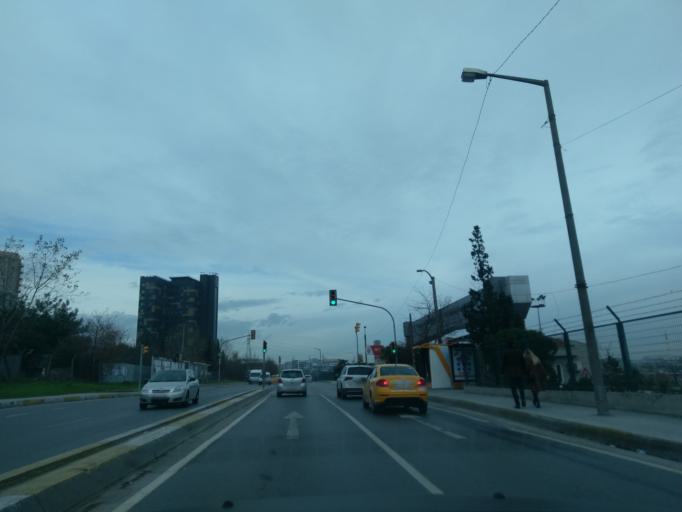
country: TR
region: Istanbul
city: Mahmutbey
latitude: 41.0580
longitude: 28.7914
